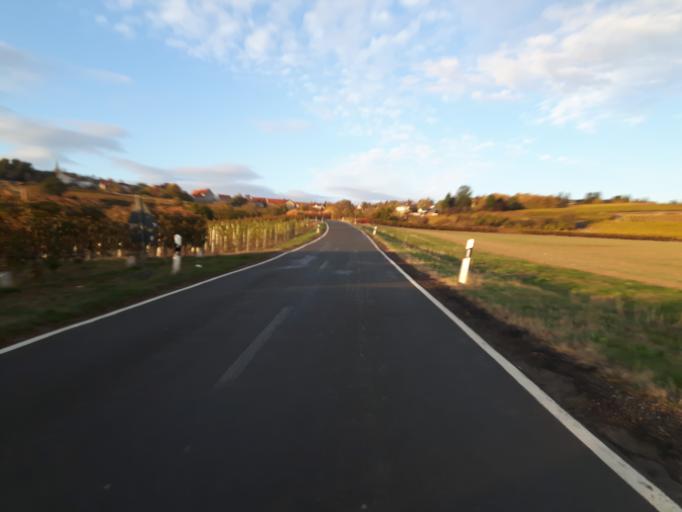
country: DE
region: Rheinland-Pfalz
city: Molsheim
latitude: 49.6410
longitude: 8.1701
